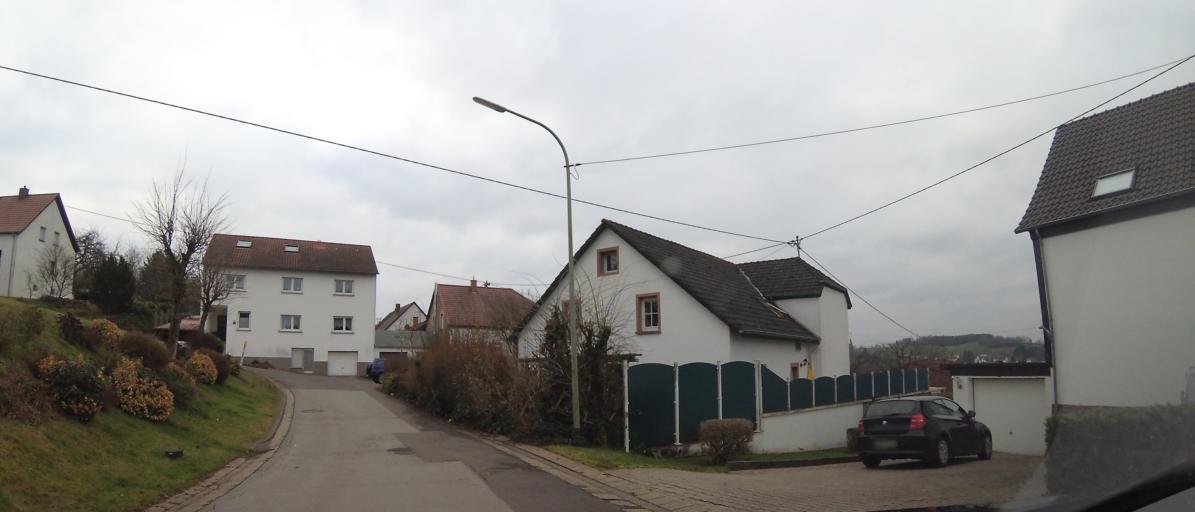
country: DE
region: Saarland
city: Illingen
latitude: 49.3885
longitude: 7.0778
